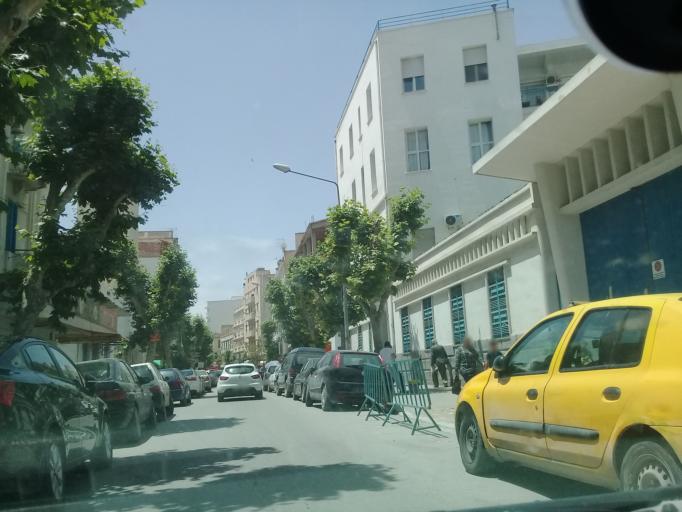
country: TN
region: Tunis
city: Tunis
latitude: 36.7944
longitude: 10.1790
